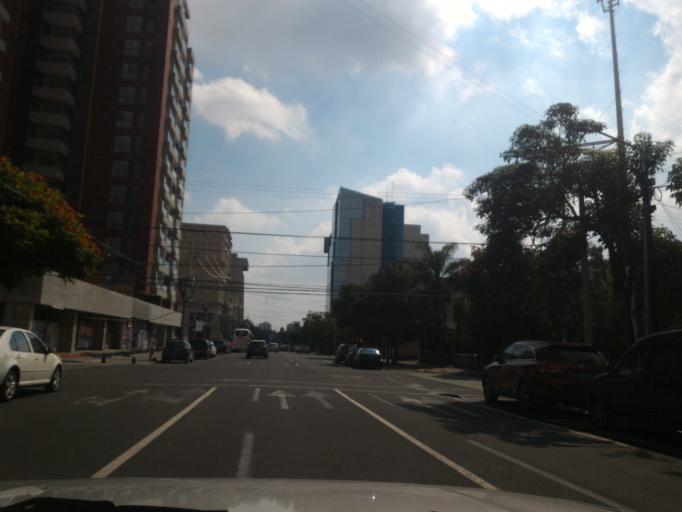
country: MX
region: Jalisco
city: Guadalajara
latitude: 20.6733
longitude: -103.3830
